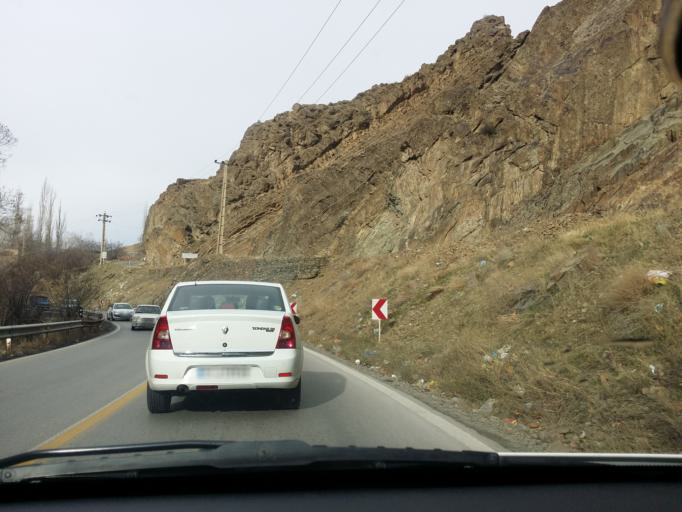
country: IR
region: Tehran
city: Tajrish
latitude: 36.0225
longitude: 51.2638
